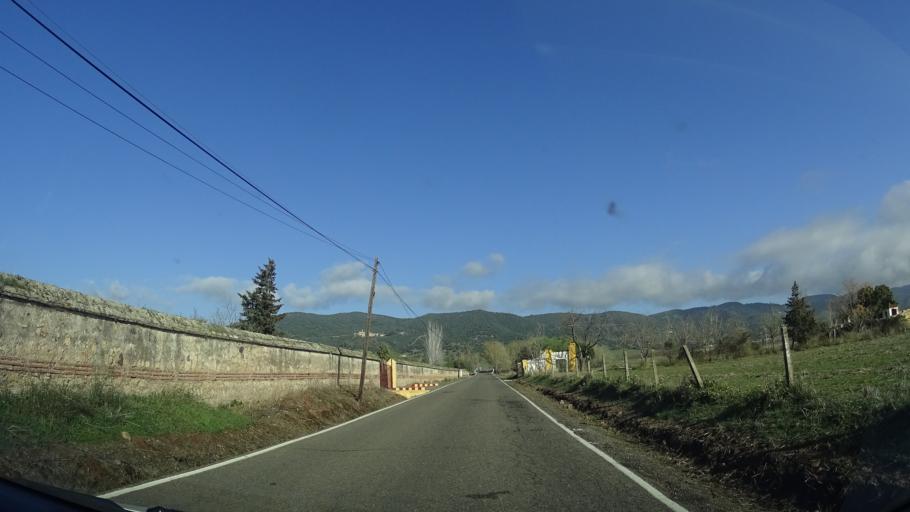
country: ES
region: Andalusia
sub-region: Province of Cordoba
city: Villarrubia
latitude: 37.8780
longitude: -4.8502
